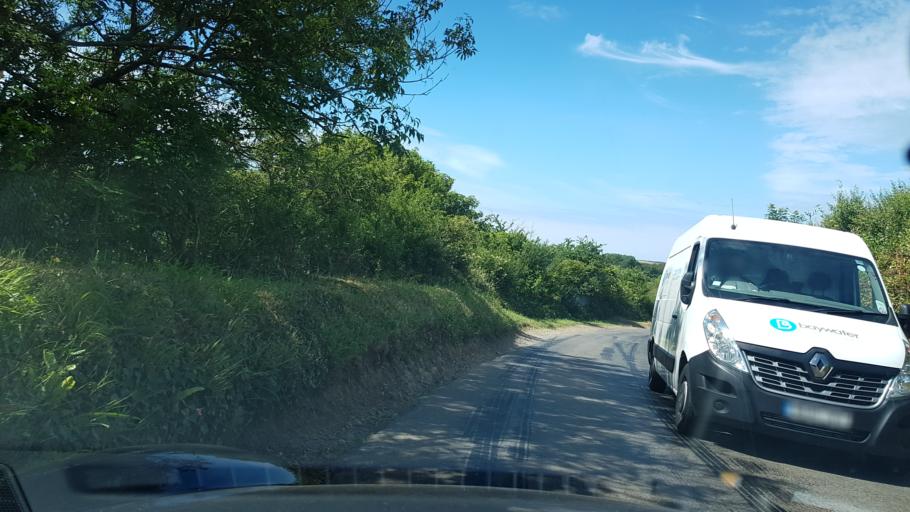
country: GB
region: Wales
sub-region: Pembrokeshire
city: Dale
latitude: 51.7393
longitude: -5.1537
